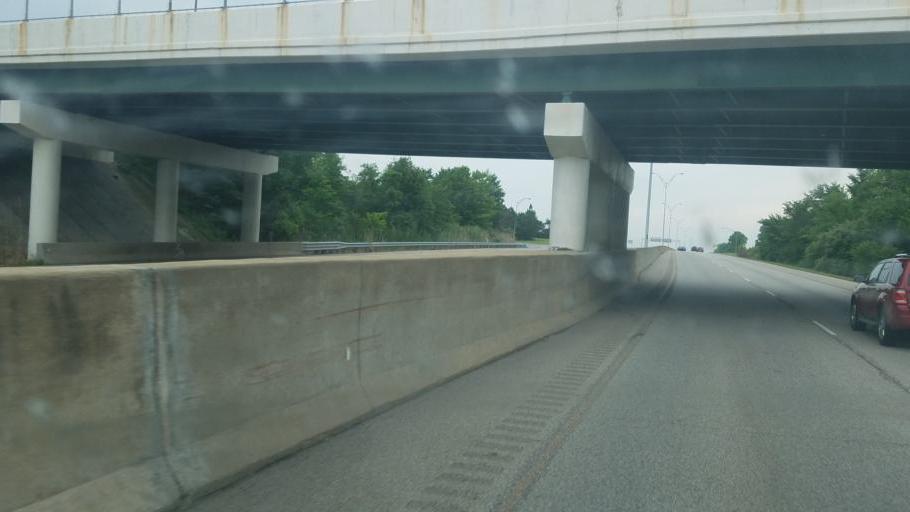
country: US
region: Ohio
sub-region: Summit County
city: Sawyerwood
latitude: 41.0260
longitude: -81.4828
